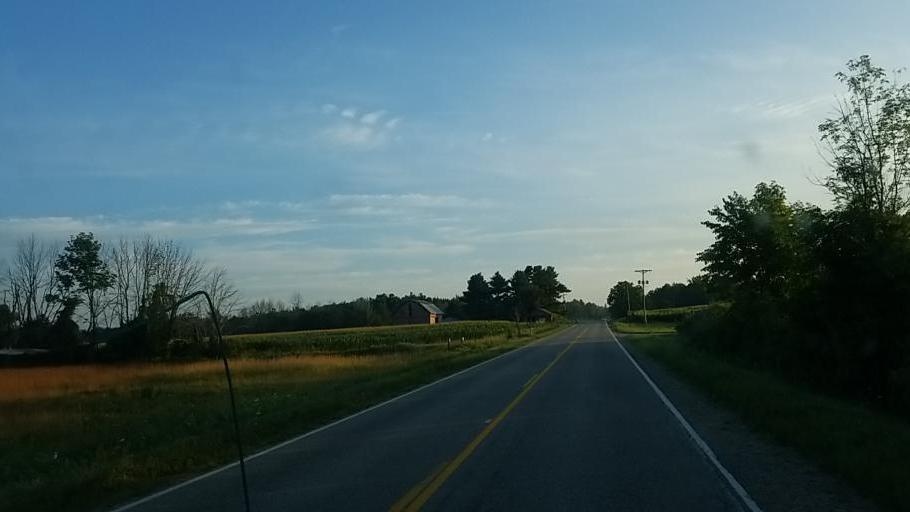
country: US
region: Michigan
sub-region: Montcalm County
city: Howard City
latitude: 43.3447
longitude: -85.4031
